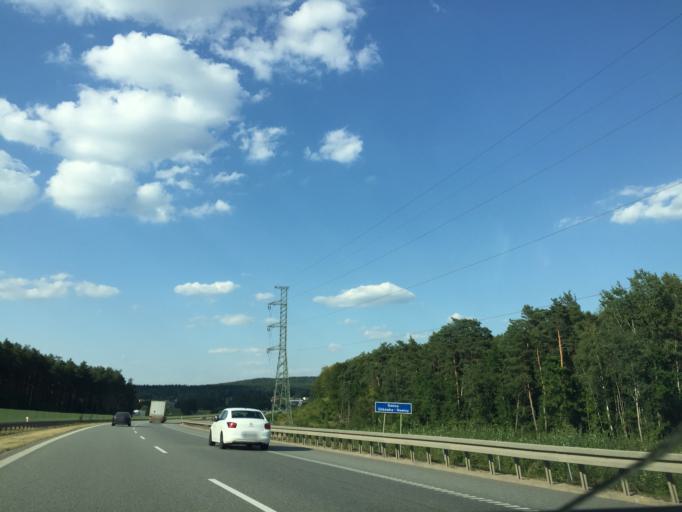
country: PL
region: Swietokrzyskie
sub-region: Powiat kielecki
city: Checiny
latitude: 50.8284
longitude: 20.4677
